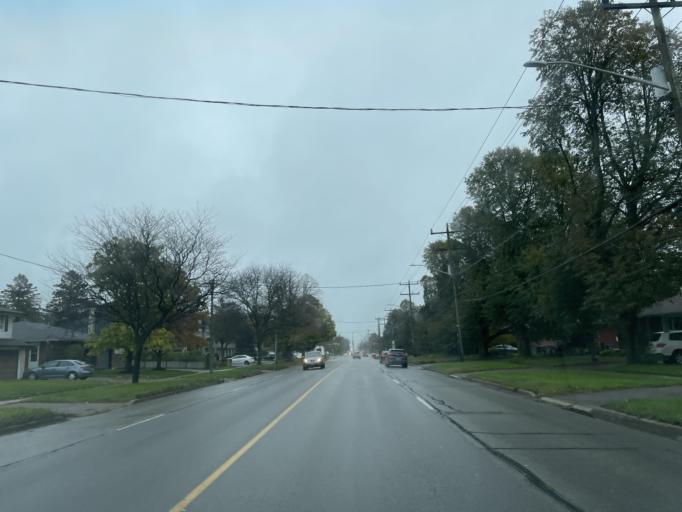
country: CA
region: Ontario
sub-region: Wellington County
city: Guelph
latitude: 43.5730
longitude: -80.2534
